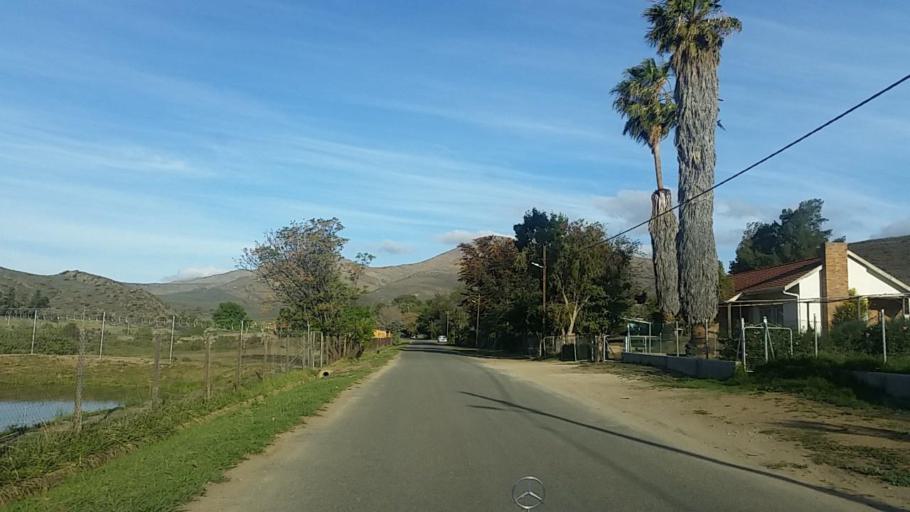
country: ZA
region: Western Cape
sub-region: Eden District Municipality
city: Knysna
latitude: -33.6537
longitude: 23.1306
